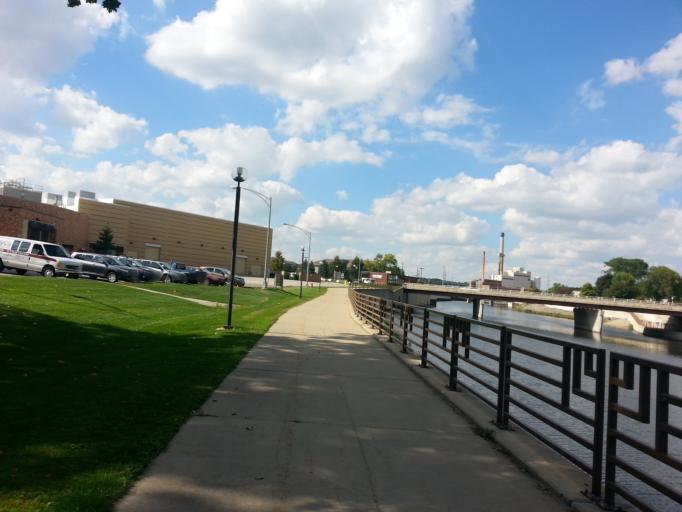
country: US
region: Minnesota
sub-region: Olmsted County
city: Rochester
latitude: 44.0223
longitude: -92.4569
